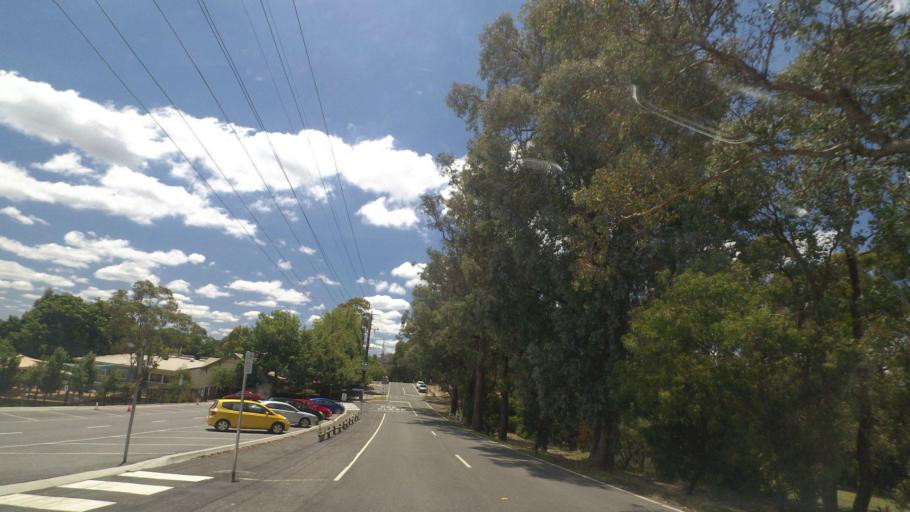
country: AU
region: Victoria
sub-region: Yarra Ranges
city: Chirnside Park
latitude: -37.7316
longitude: 145.2738
